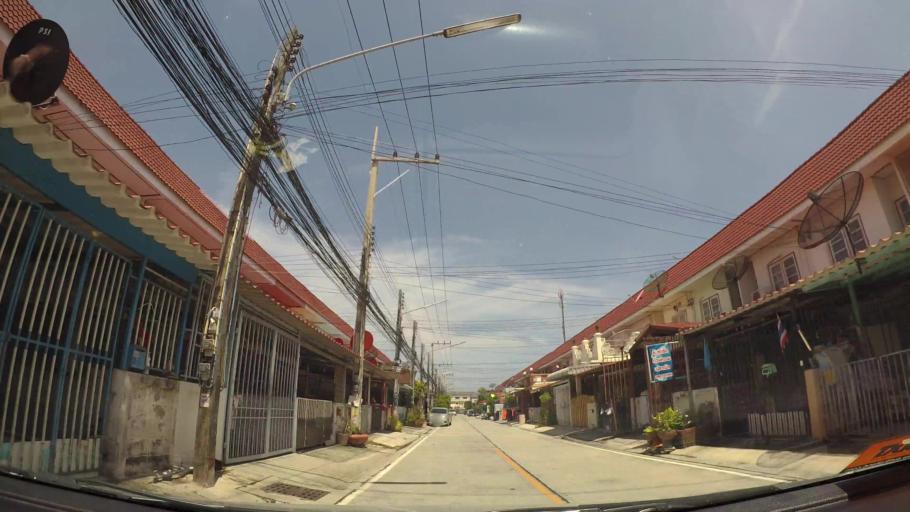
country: TH
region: Chon Buri
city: Chon Buri
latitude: 13.3296
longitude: 100.9480
